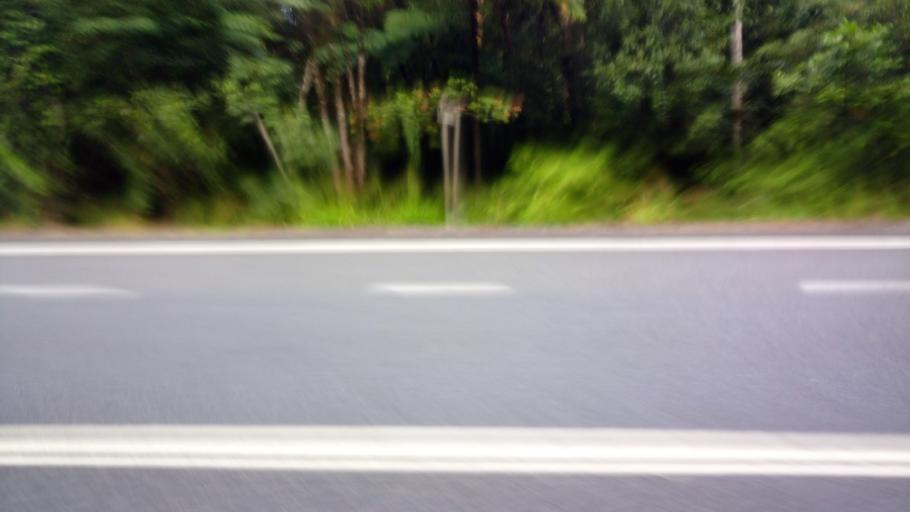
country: AU
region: Queensland
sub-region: Tablelands
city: Ravenshoe
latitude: -17.5836
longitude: 145.6959
